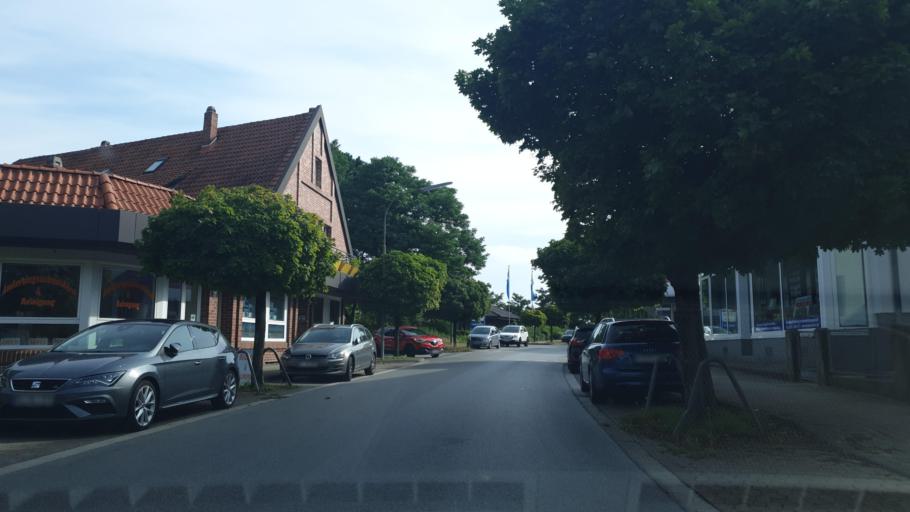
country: DE
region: North Rhine-Westphalia
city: Bad Oeynhausen
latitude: 52.1992
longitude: 8.7590
